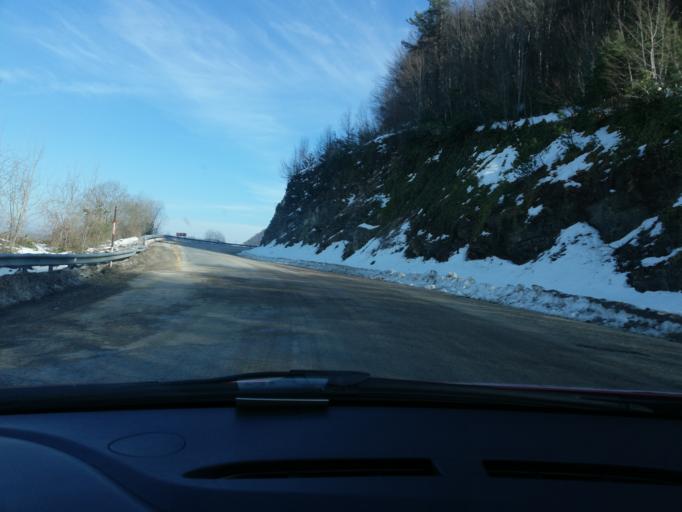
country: TR
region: Kastamonu
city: Cide
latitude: 41.8571
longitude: 33.0629
